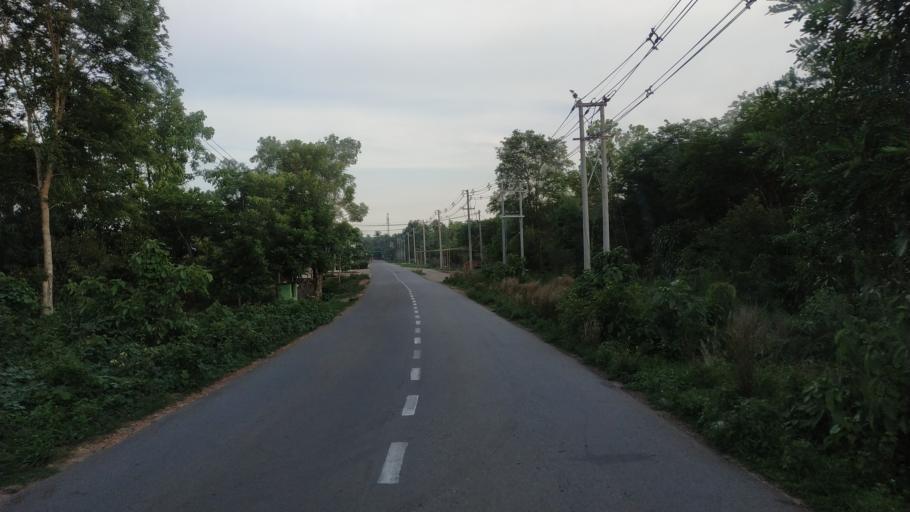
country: MM
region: Mon
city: Kyaikto
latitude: 17.4088
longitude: 97.0731
